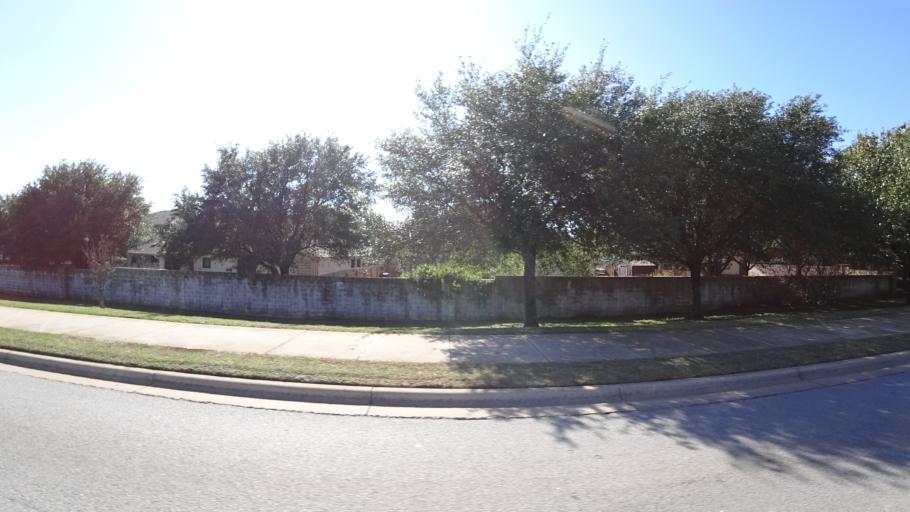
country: US
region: Texas
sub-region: Travis County
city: Shady Hollow
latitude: 30.1962
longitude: -97.8601
